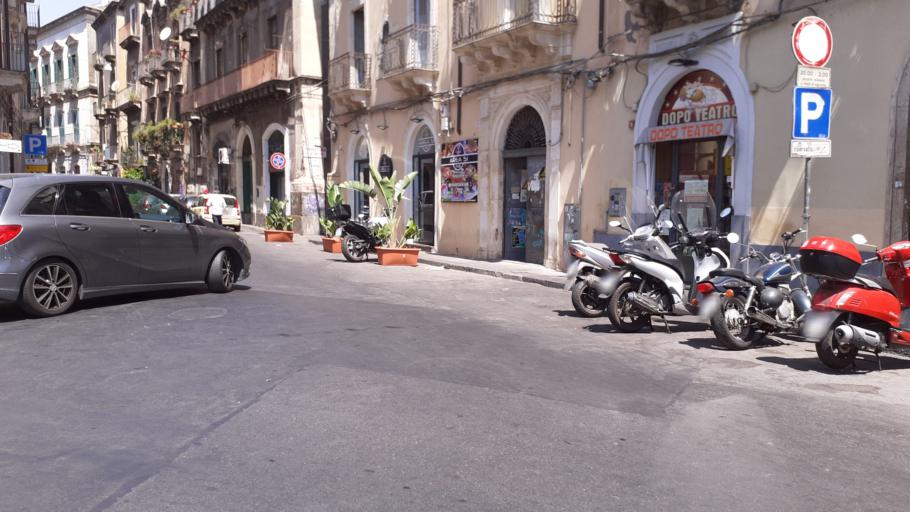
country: IT
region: Sicily
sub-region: Catania
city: Catania
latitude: 37.5050
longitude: 15.0902
